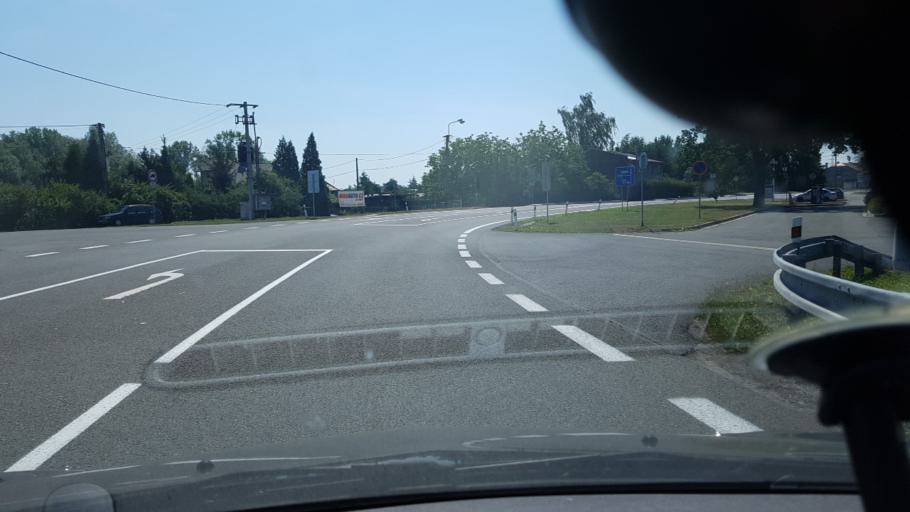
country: CZ
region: Moravskoslezsky
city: Stary Bohumin
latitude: 49.9096
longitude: 18.3372
